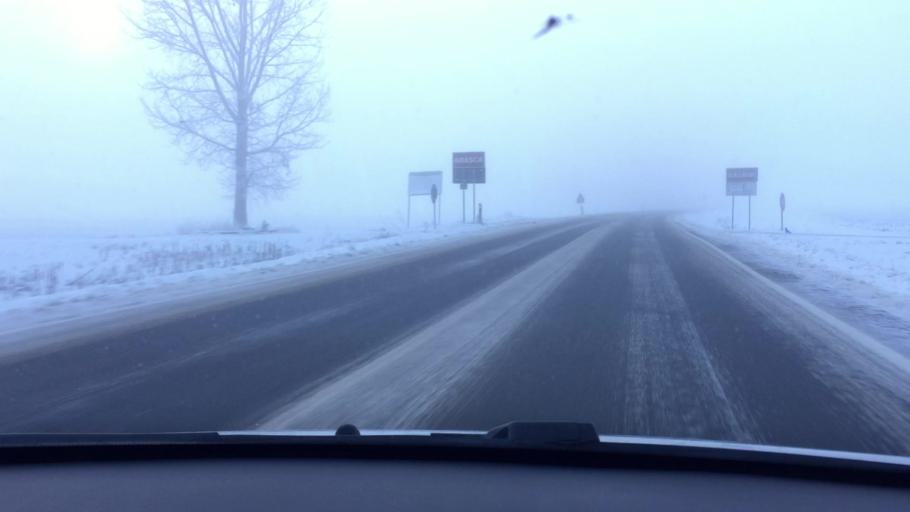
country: IT
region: Piedmont
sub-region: Provincia di Torino
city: Airasca
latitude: 44.9055
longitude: 7.4909
